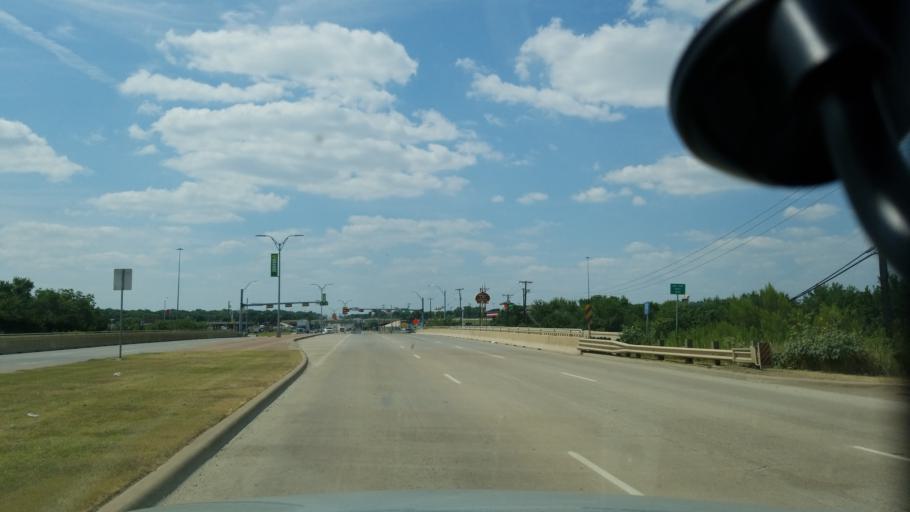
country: US
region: Texas
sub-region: Dallas County
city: Grand Prairie
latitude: 32.7637
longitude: -96.9950
